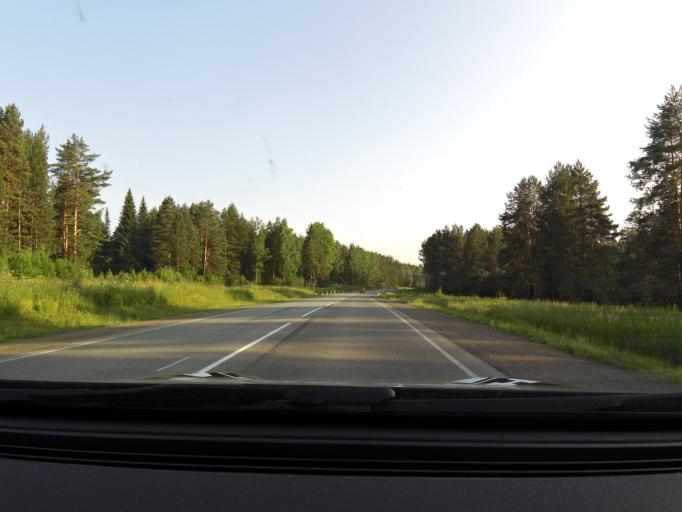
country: RU
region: Sverdlovsk
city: Nizhniye Sergi
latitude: 56.5907
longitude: 59.2262
